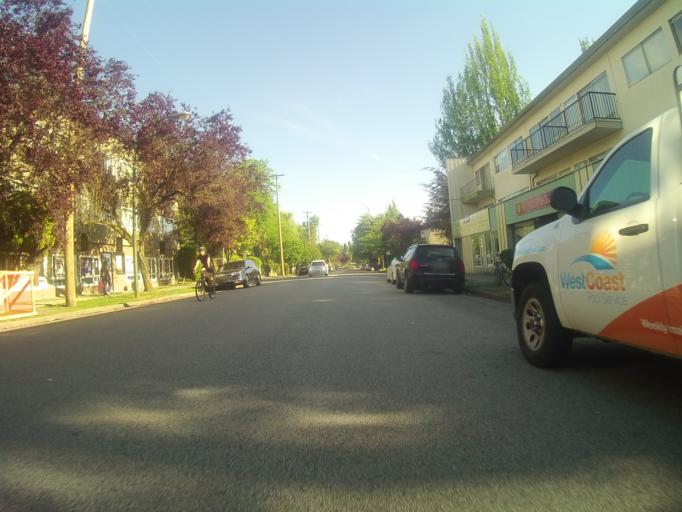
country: CA
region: British Columbia
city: Vancouver
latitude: 49.2565
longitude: -123.1201
